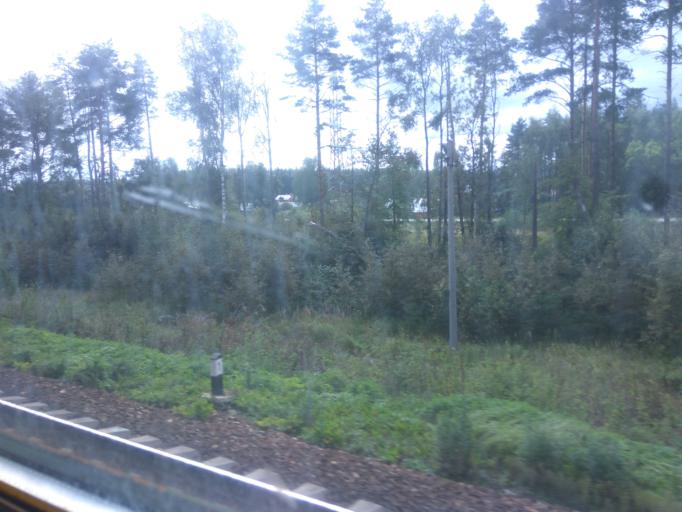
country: RU
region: Moskovskaya
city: Malyshevo
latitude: 55.4868
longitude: 38.3917
